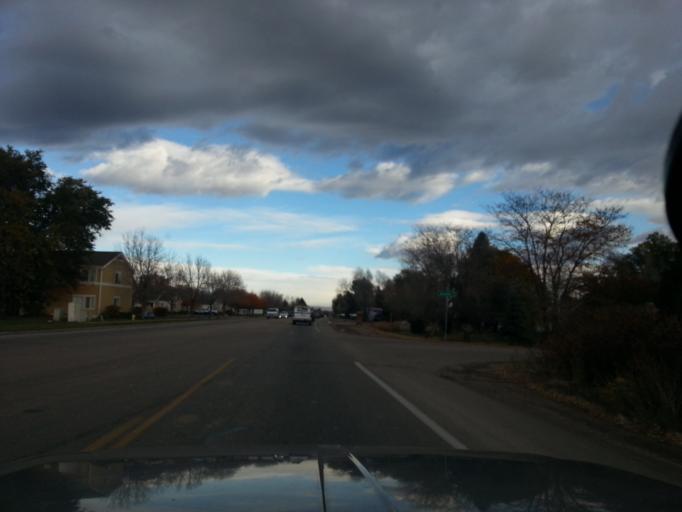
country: US
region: Colorado
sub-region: Larimer County
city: Fort Collins
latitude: 40.5323
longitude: -105.1153
